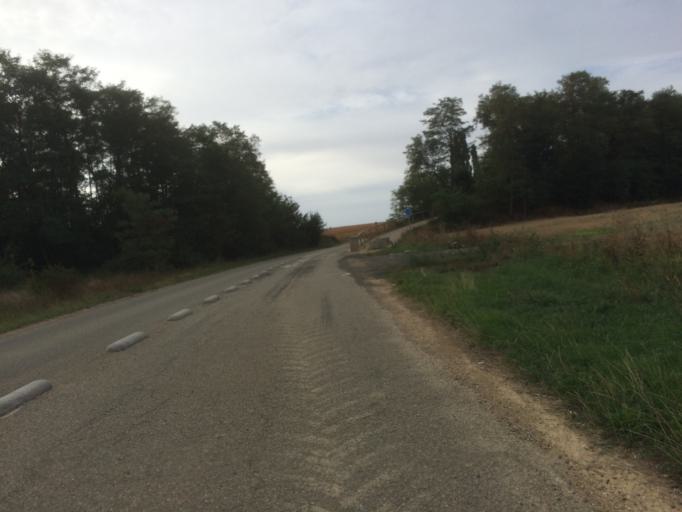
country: FR
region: Ile-de-France
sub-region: Departement de l'Essonne
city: Gometz-la-Ville
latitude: 48.6677
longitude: 2.1177
